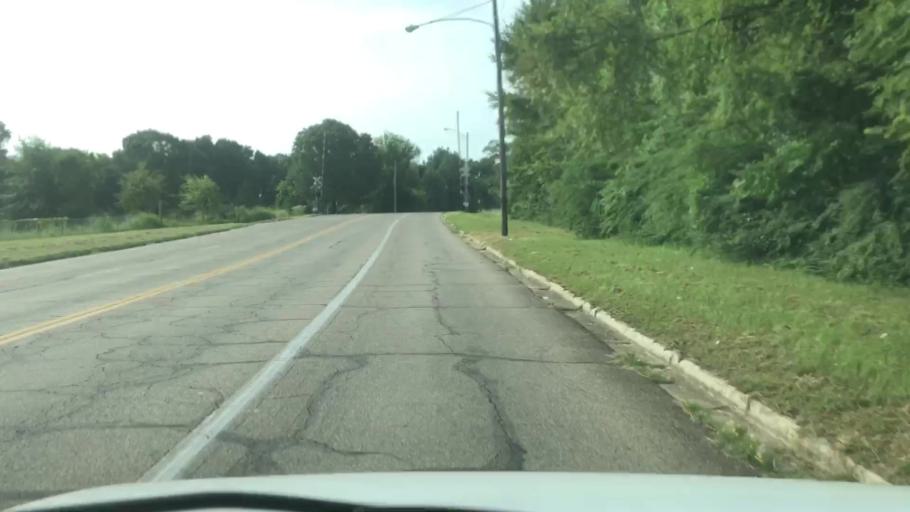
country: US
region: Texas
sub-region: Bowie County
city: Wake Village
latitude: 33.4087
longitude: -94.0802
